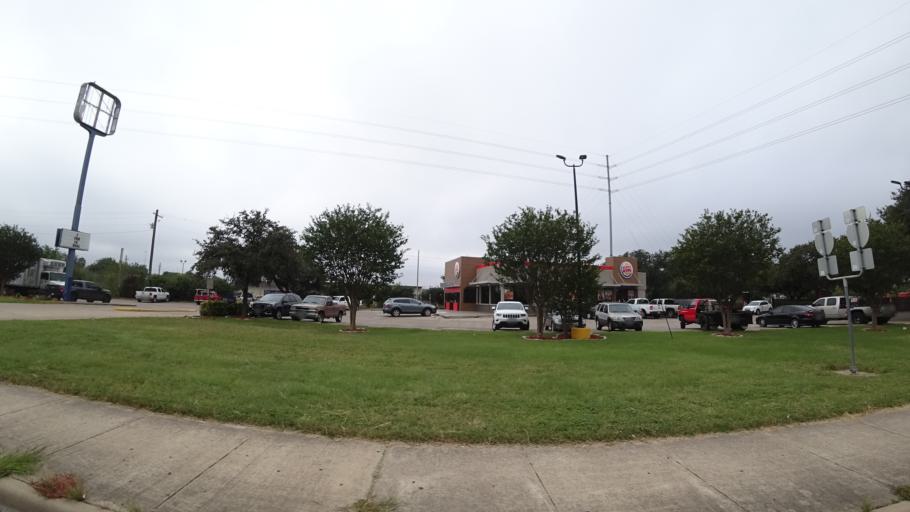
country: US
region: Texas
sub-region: Travis County
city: Austin
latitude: 30.2170
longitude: -97.7545
